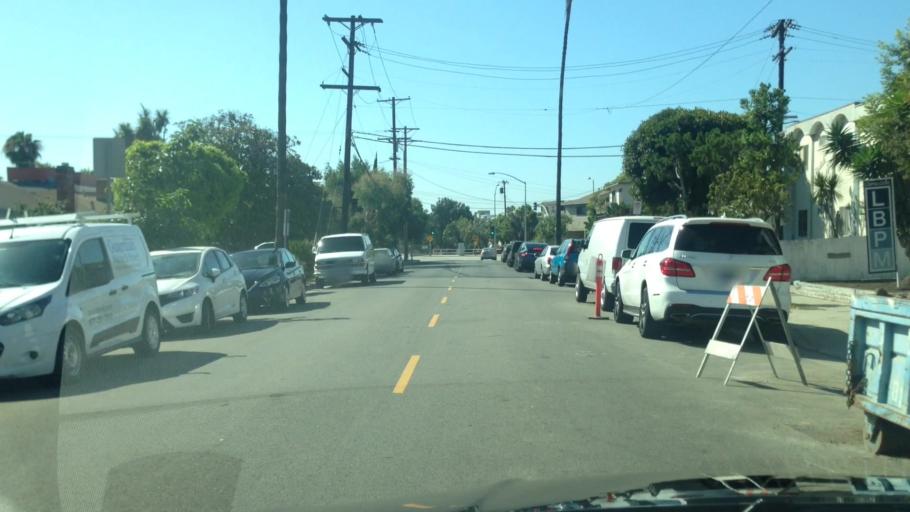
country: US
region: California
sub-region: Los Angeles County
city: Culver City
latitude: 34.0010
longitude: -118.4186
